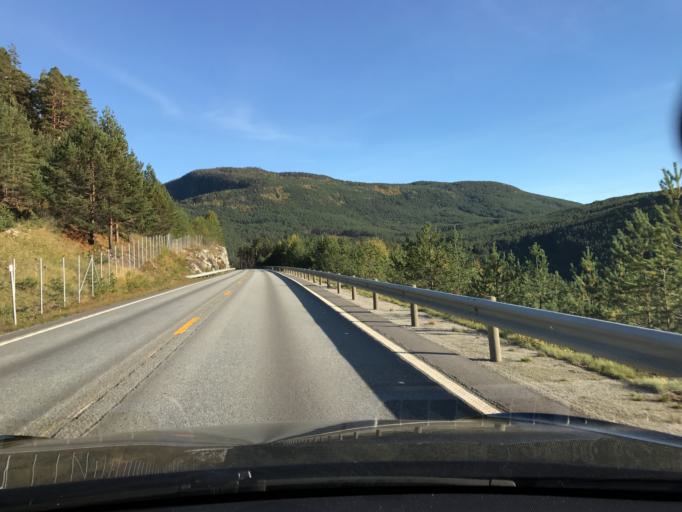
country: NO
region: Sogn og Fjordane
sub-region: Sogndal
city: Sogndalsfjora
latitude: 61.1821
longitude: 7.2743
